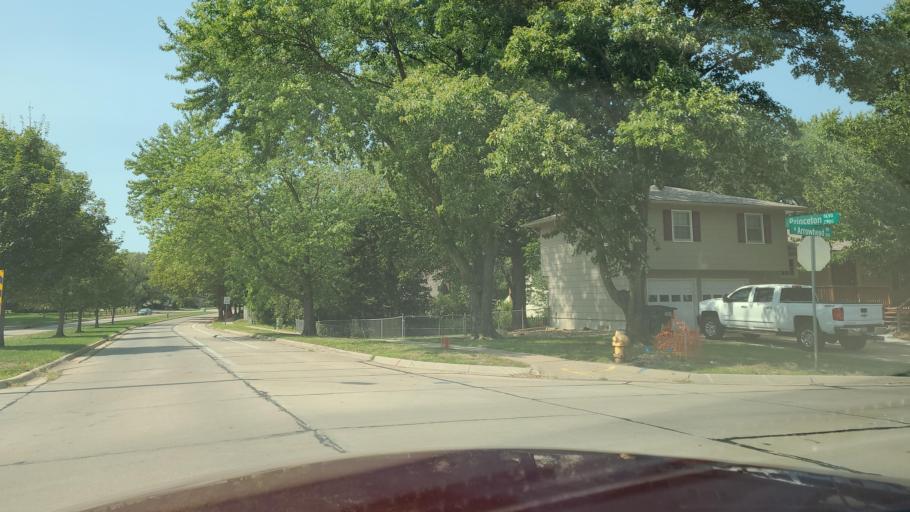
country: US
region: Kansas
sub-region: Douglas County
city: Lawrence
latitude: 38.9838
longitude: -95.2716
